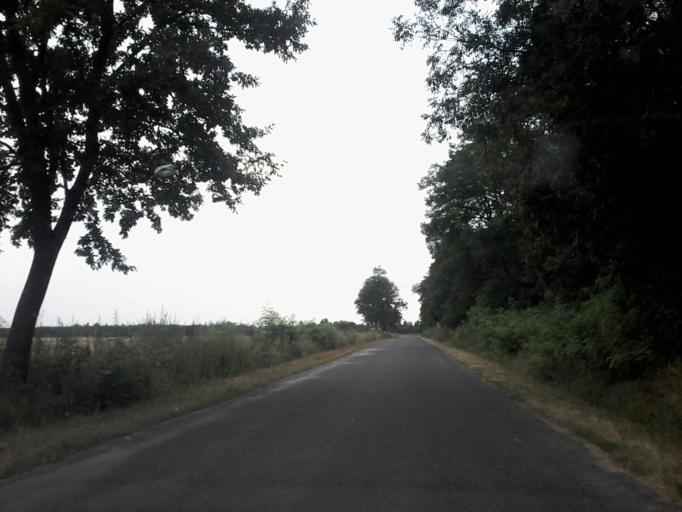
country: HU
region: Vas
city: Celldomolk
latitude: 47.2078
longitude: 17.0798
